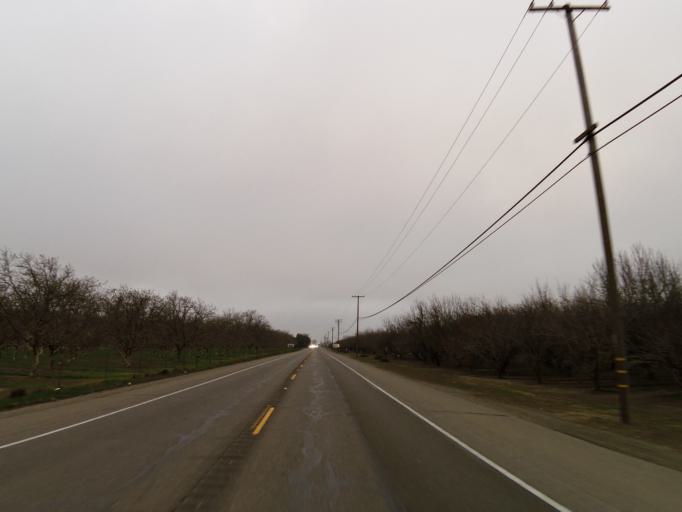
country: US
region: California
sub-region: Stanislaus County
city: Riverdale Park
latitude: 37.6380
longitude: -121.1137
